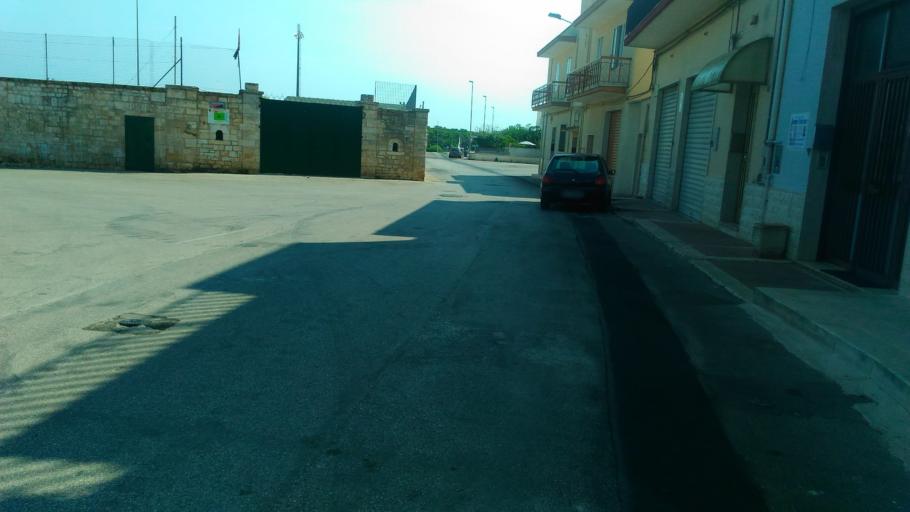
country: IT
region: Apulia
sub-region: Provincia di Bari
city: Locorotondo
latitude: 40.7526
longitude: 17.3344
